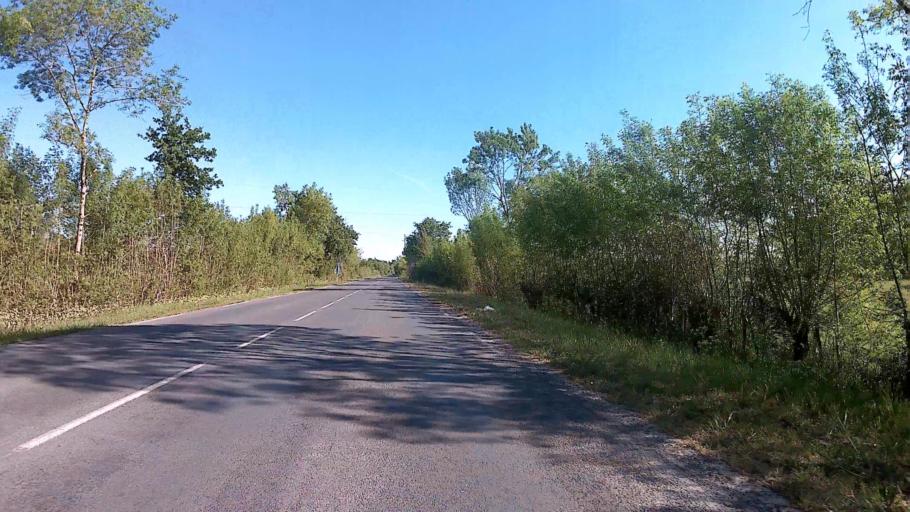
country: FR
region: Aquitaine
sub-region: Departement de la Gironde
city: Cadaujac
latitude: 44.7660
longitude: -0.5286
